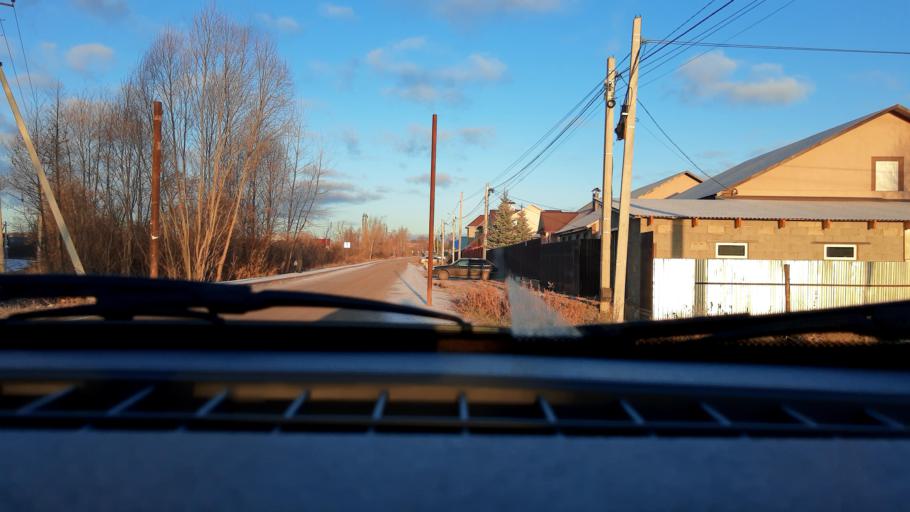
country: RU
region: Bashkortostan
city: Mikhaylovka
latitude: 54.7837
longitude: 55.8192
